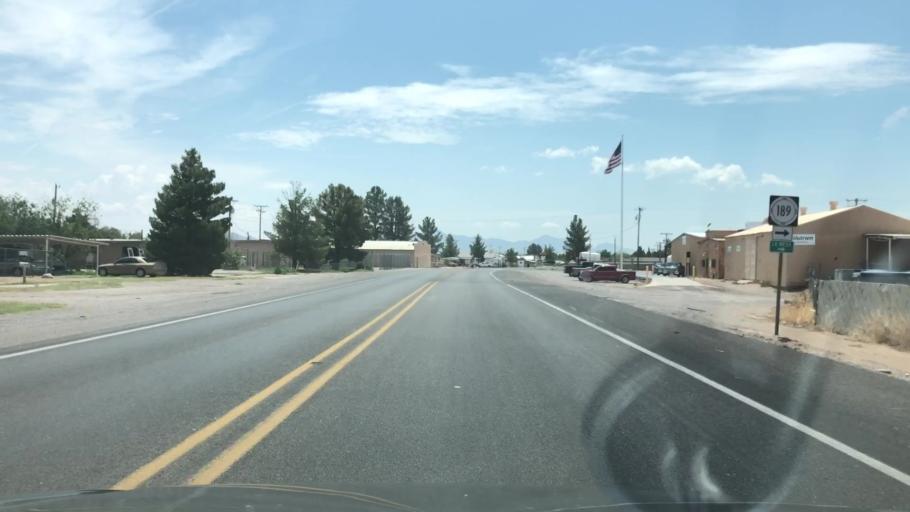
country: US
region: New Mexico
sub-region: Dona Ana County
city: Vado
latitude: 32.1167
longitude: -106.6660
